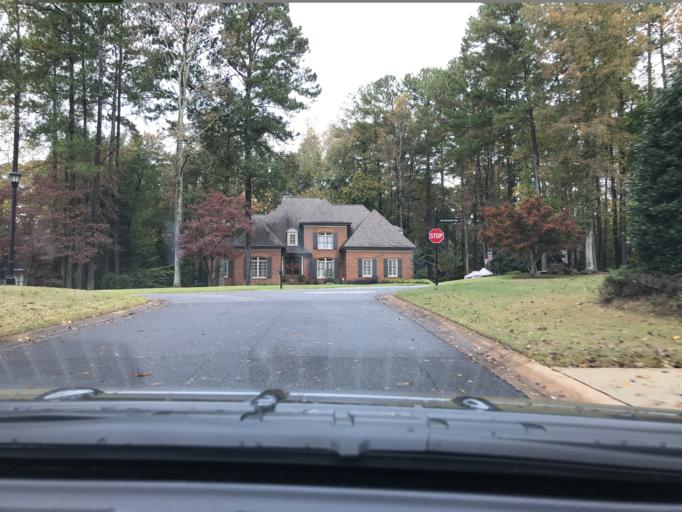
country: US
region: Georgia
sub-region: Fulton County
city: Johns Creek
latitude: 34.0047
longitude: -84.2415
